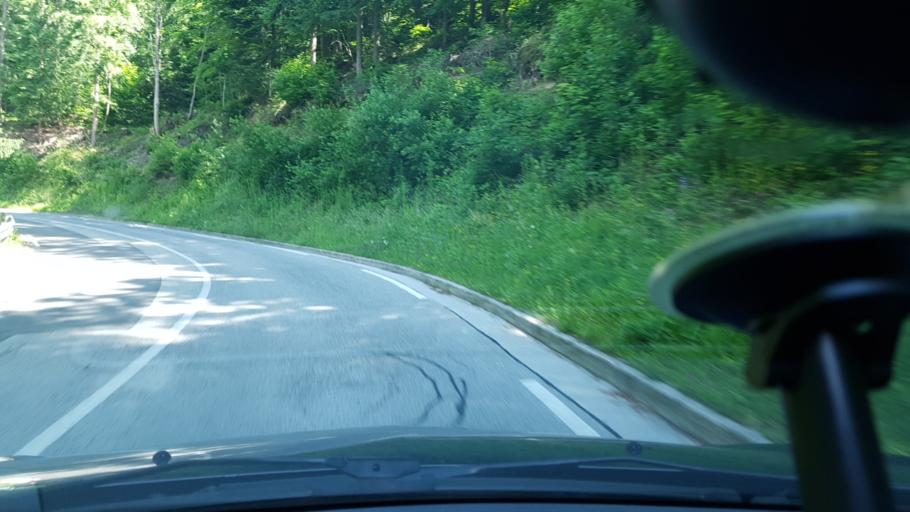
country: SI
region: Zrece
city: Zrece
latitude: 46.4036
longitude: 15.3707
